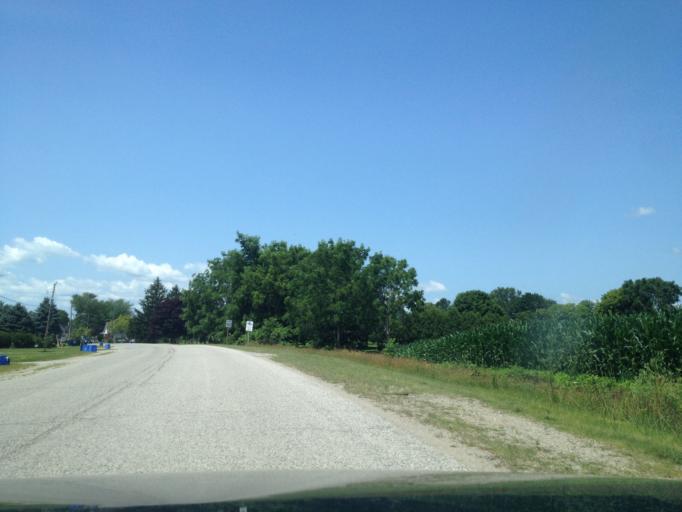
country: CA
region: Ontario
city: Aylmer
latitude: 42.6463
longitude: -80.7962
